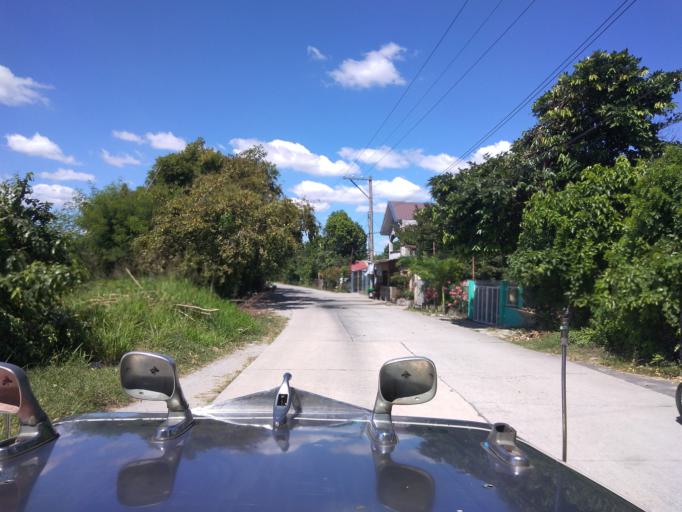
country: PH
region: Central Luzon
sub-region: Province of Pampanga
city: Magliman
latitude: 15.0298
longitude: 120.6497
